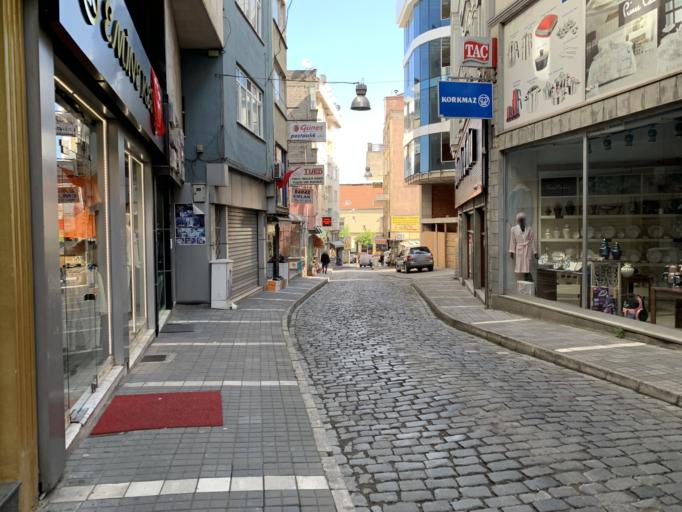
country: TR
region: Trabzon
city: Trabzon
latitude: 41.0057
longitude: 39.7226
